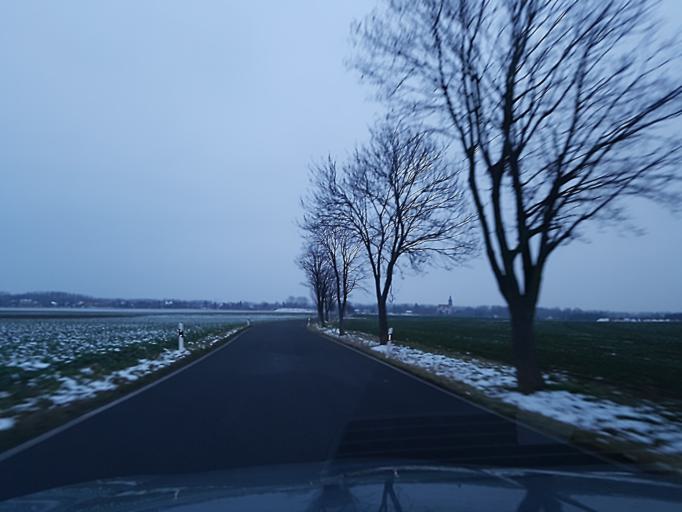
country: DE
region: Saxony
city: Stauchitz
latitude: 51.2700
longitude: 13.2220
